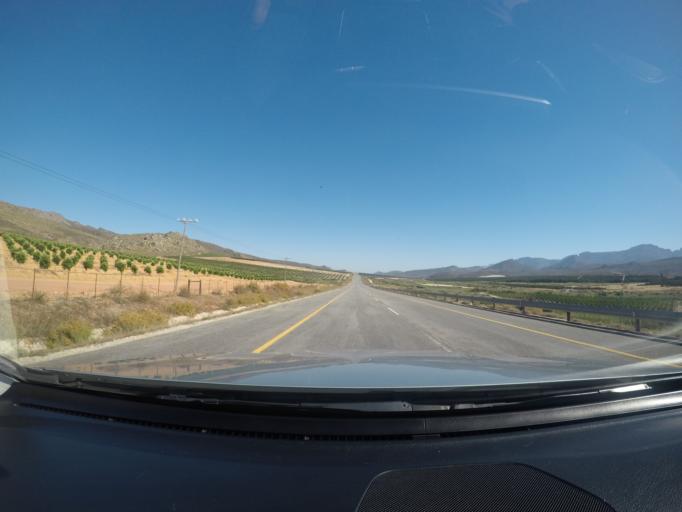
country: ZA
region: Western Cape
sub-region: West Coast District Municipality
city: Clanwilliam
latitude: -32.4960
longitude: 18.9661
